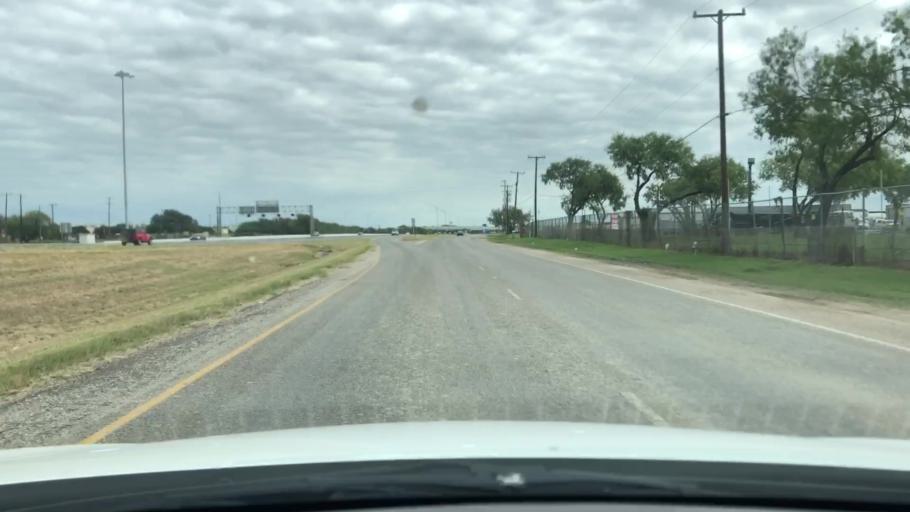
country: US
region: Texas
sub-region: Bexar County
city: Lackland Air Force Base
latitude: 29.4071
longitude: -98.5979
